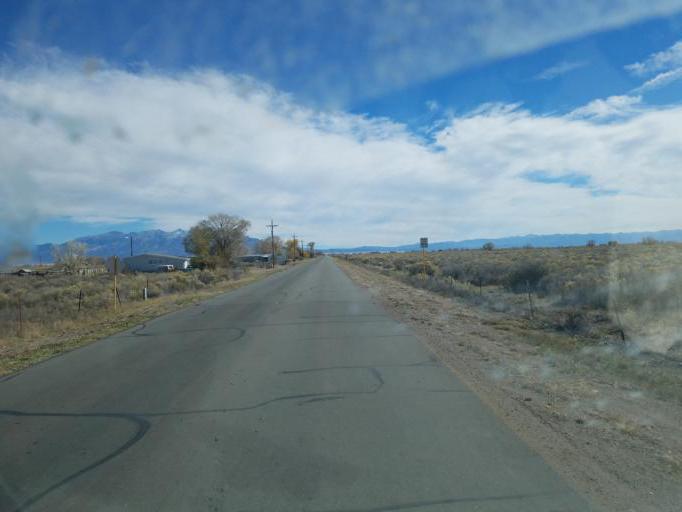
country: US
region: Colorado
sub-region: Alamosa County
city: Alamosa East
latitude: 37.5024
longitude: -105.8551
